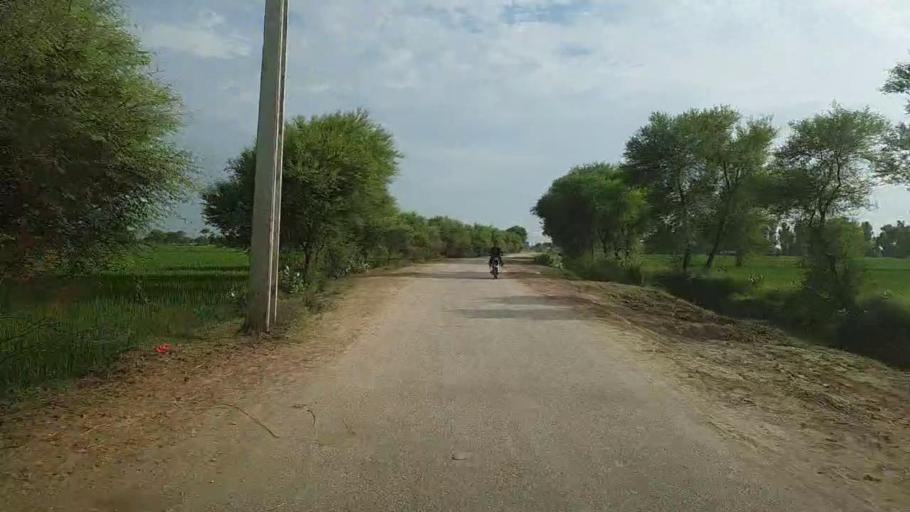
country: PK
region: Sindh
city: Thul
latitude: 28.2572
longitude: 68.8581
